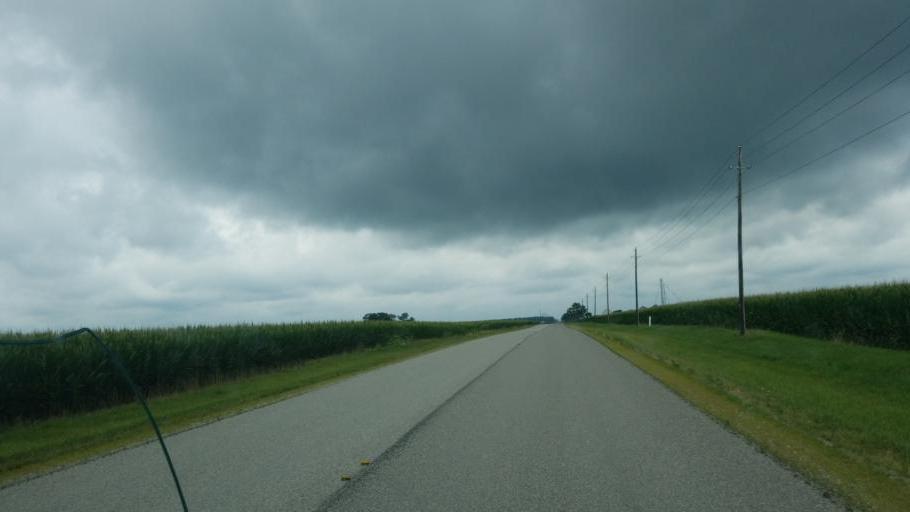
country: US
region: Indiana
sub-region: Adams County
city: Berne
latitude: 40.6555
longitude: -85.0732
